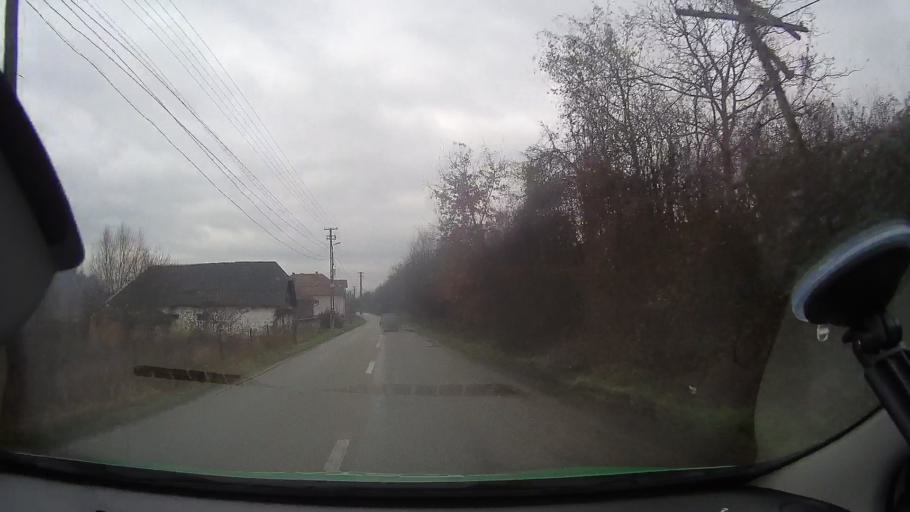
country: RO
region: Arad
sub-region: Comuna Gurahont
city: Gurahont
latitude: 46.2644
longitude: 22.3415
